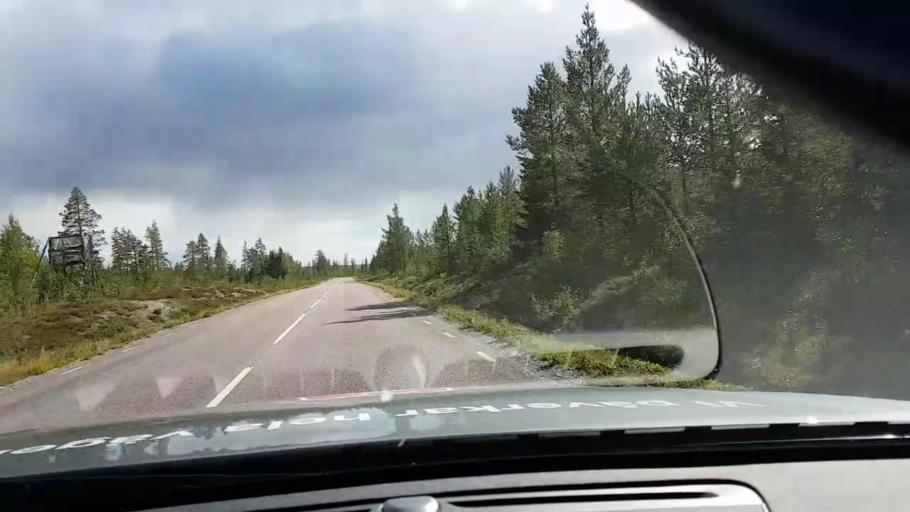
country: SE
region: Vaesterbotten
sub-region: Asele Kommun
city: Asele
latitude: 63.8991
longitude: 17.3489
